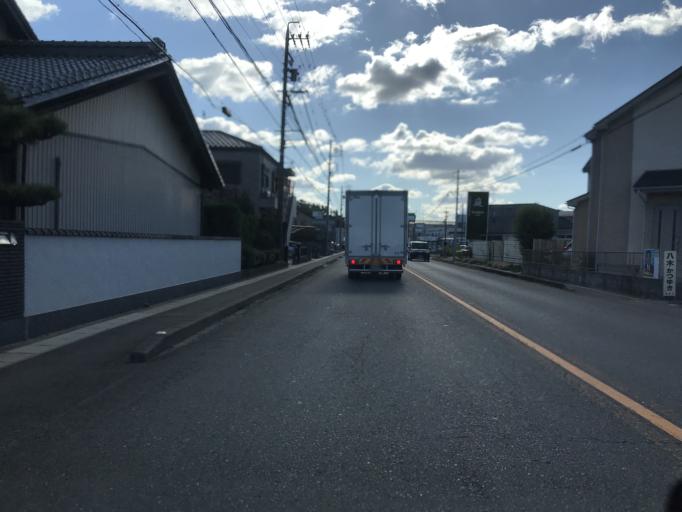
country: JP
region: Aichi
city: Inazawa
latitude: 35.2234
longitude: 136.8413
